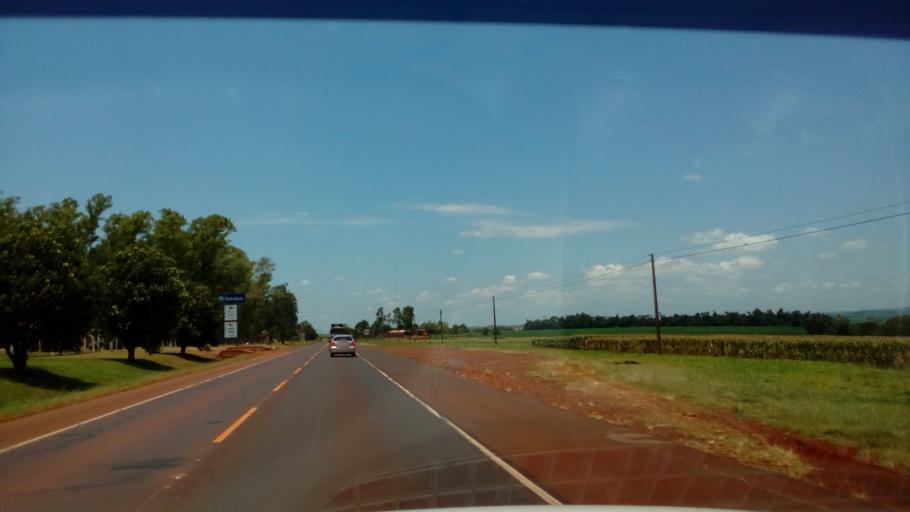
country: PY
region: Alto Parana
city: Santa Rita
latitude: -25.8632
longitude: -55.1177
